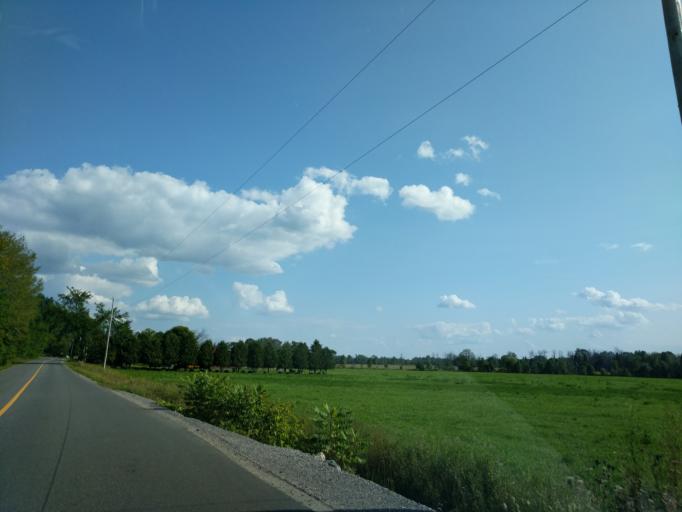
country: CA
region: Quebec
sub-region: Outaouais
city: Wakefield
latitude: 45.5015
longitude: -75.9207
